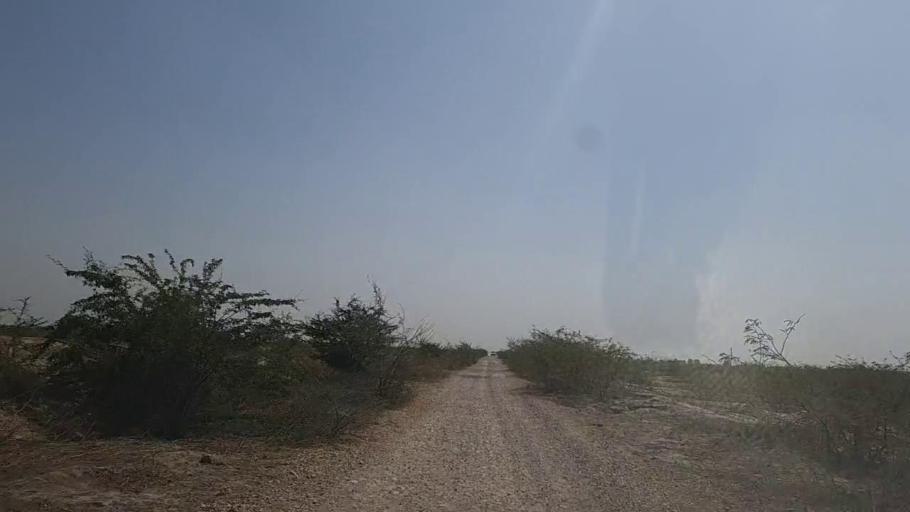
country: PK
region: Sindh
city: Naukot
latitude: 24.6382
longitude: 69.2736
